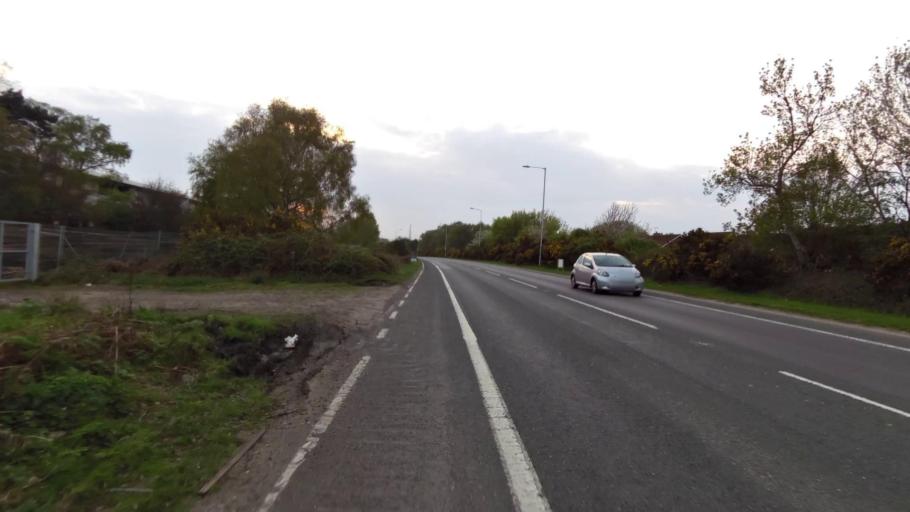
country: GB
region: England
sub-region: Suffolk
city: Kesgrave
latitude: 52.0345
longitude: 1.2122
